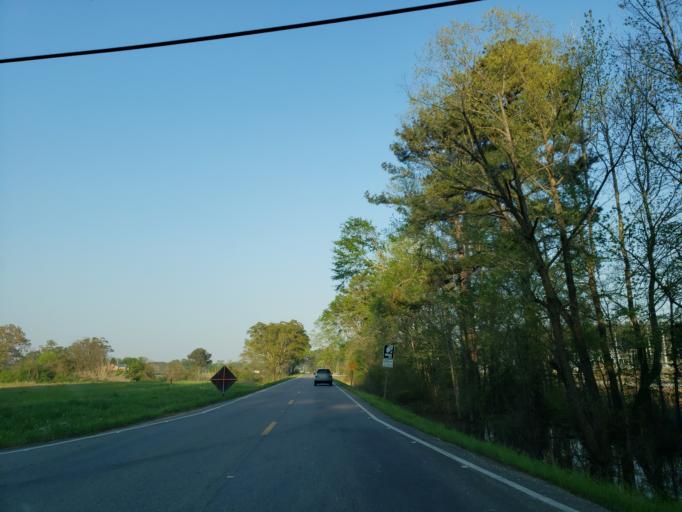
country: US
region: Mississippi
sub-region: Lauderdale County
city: Marion
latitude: 32.3955
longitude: -88.6196
